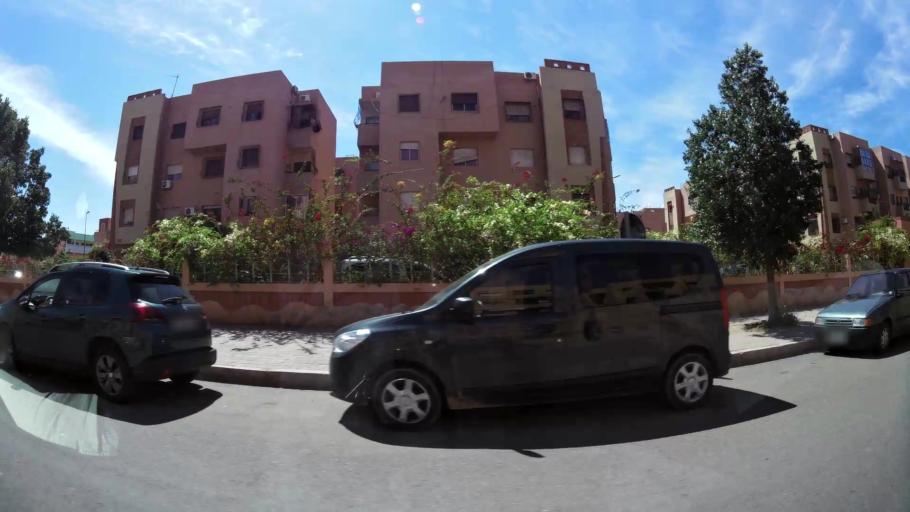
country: MA
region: Marrakech-Tensift-Al Haouz
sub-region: Marrakech
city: Marrakesh
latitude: 31.6405
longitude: -8.0787
